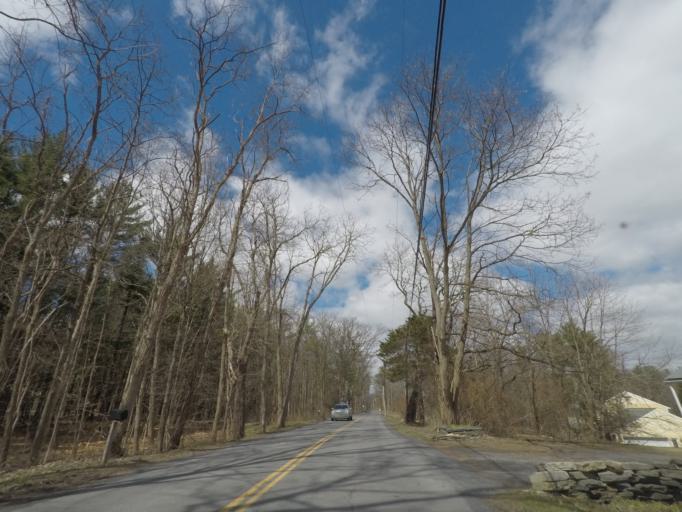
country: US
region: New York
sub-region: Albany County
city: Voorheesville
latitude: 42.6315
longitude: -73.9272
